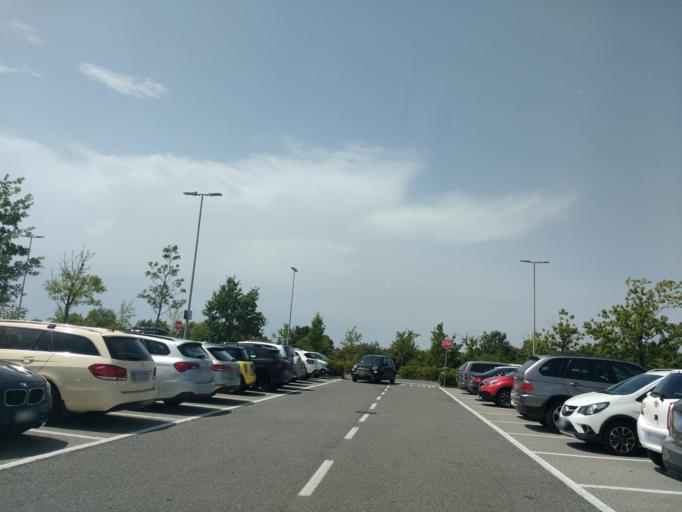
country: IT
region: Latium
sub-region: Citta metropolitana di Roma Capitale
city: Selcetta
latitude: 41.7189
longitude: 12.4442
